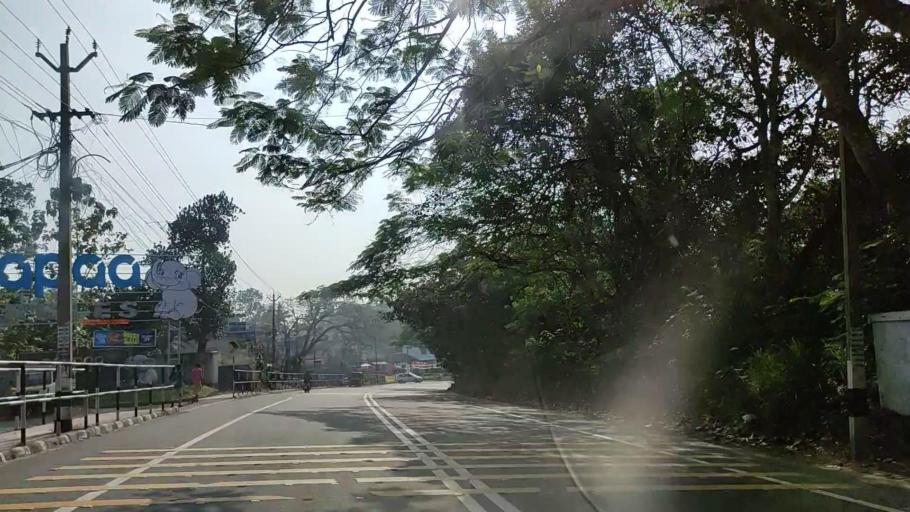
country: IN
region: Kerala
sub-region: Kollam
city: Punalur
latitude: 8.9788
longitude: 76.8135
